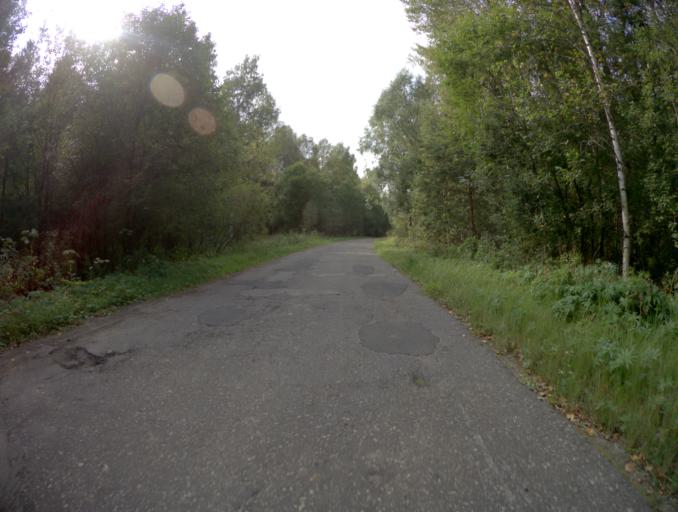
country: RU
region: Vladimir
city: Golovino
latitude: 55.9676
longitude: 40.4050
